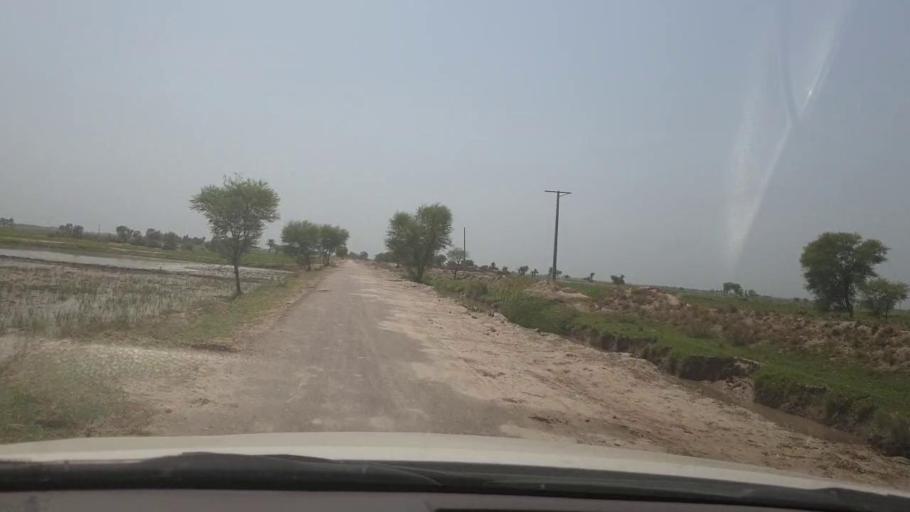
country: PK
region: Sindh
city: Shikarpur
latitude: 28.0433
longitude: 68.5665
